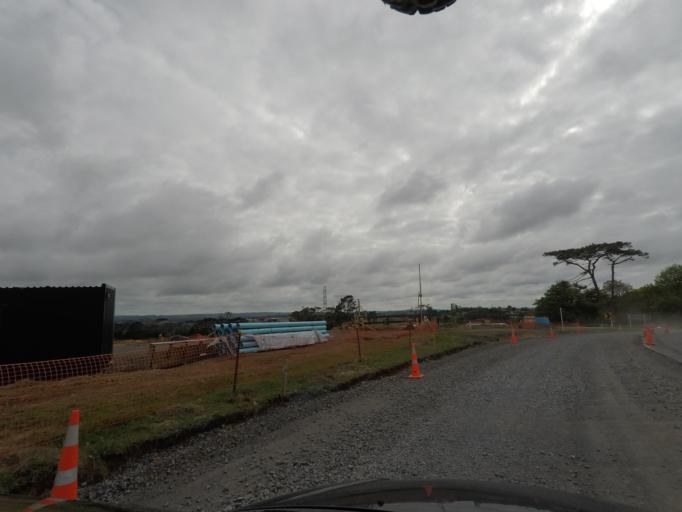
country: NZ
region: Auckland
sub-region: Auckland
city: Rosebank
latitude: -36.8359
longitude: 174.5952
